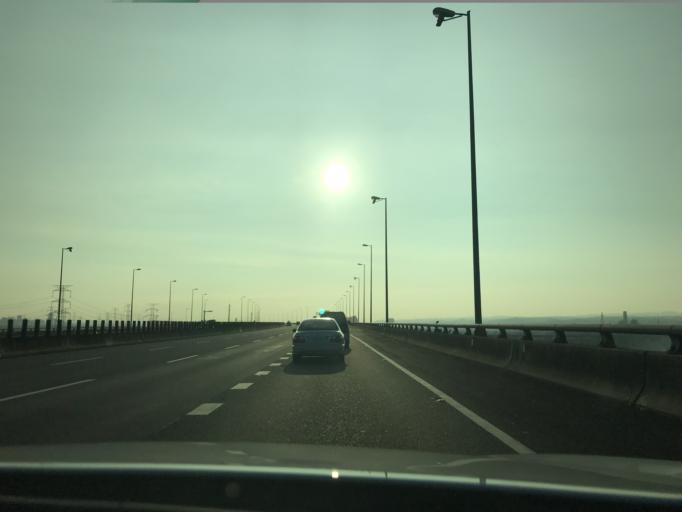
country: TW
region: Taiwan
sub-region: Changhua
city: Chang-hua
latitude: 24.1093
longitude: 120.5487
